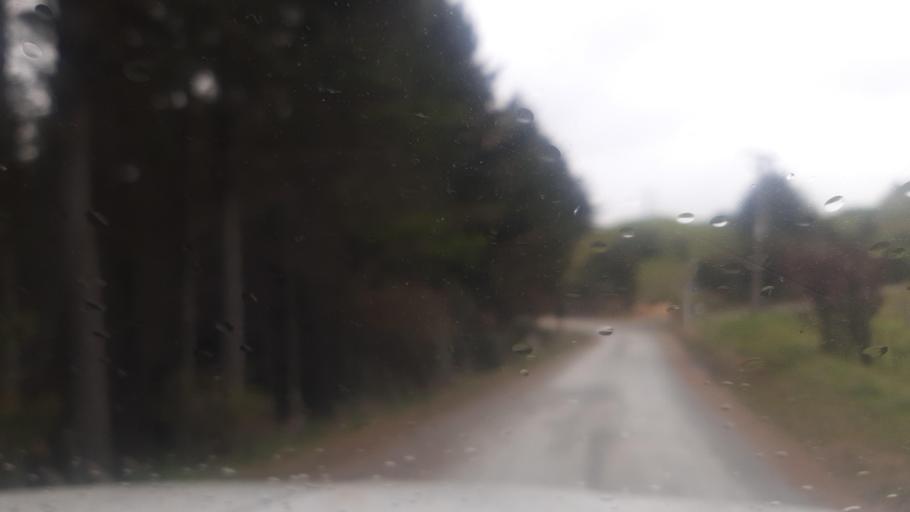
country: NZ
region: Northland
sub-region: Far North District
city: Taipa
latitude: -35.0823
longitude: 173.3898
